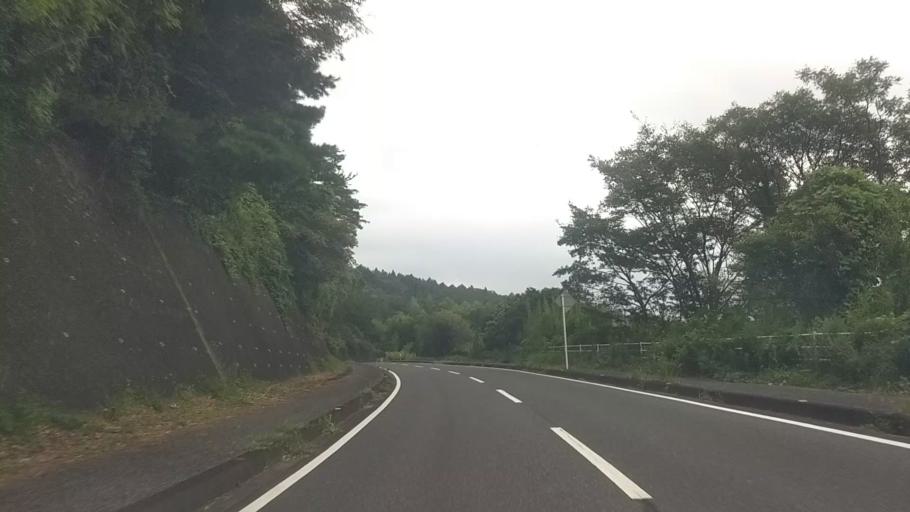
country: JP
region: Chiba
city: Kawaguchi
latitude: 35.2401
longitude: 140.0840
